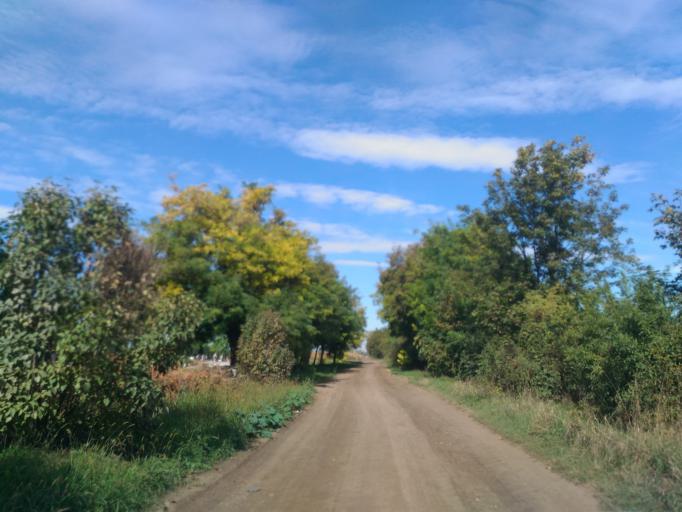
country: HU
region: Fejer
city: Pusztaszabolcs
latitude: 47.1370
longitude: 18.7807
